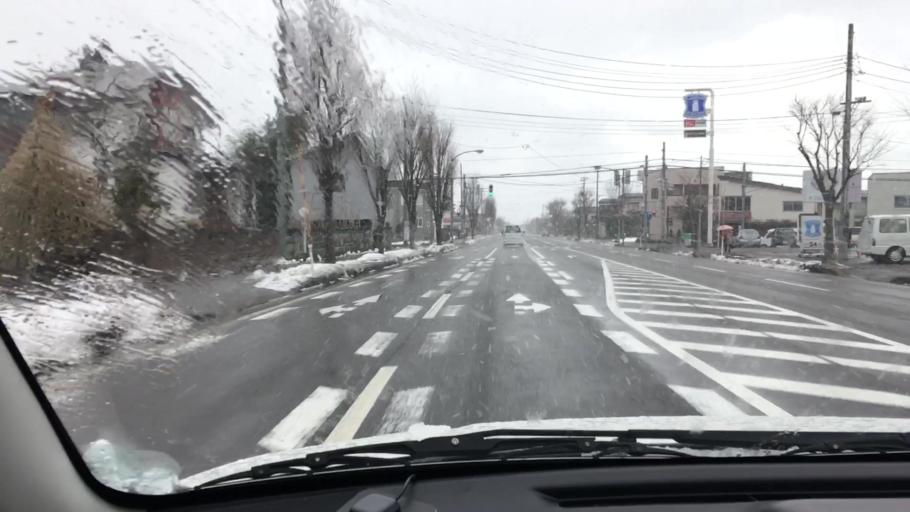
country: JP
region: Niigata
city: Joetsu
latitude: 37.1169
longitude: 138.2329
